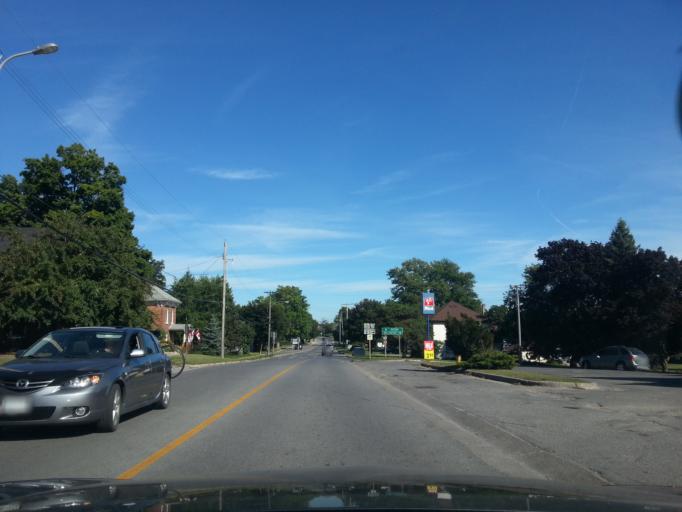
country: CA
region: Ontario
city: Prince Edward
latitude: 43.9864
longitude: -77.2392
